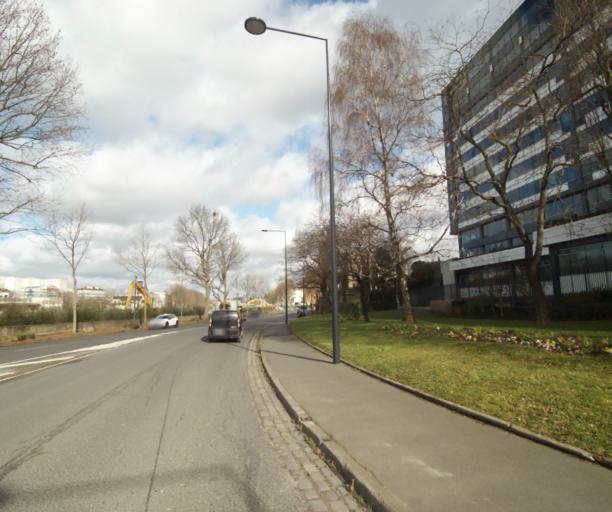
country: FR
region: Ile-de-France
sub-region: Departement de Seine-Saint-Denis
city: Saint-Denis
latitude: 48.9298
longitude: 2.3410
